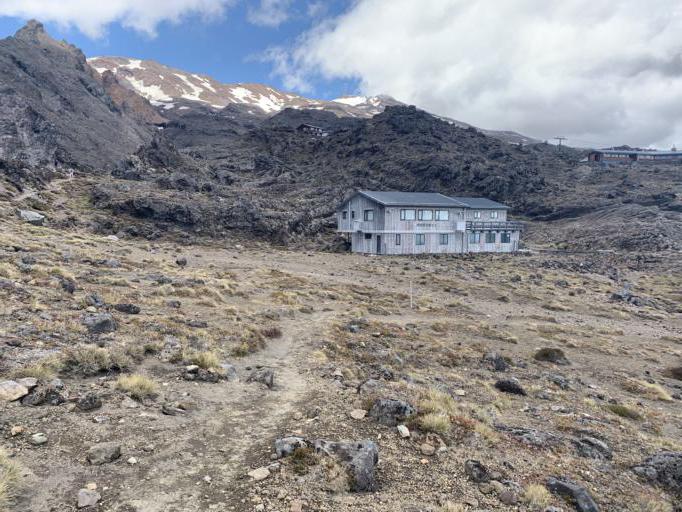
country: NZ
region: Manawatu-Wanganui
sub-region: Ruapehu District
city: Waiouru
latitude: -39.2364
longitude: 175.5609
